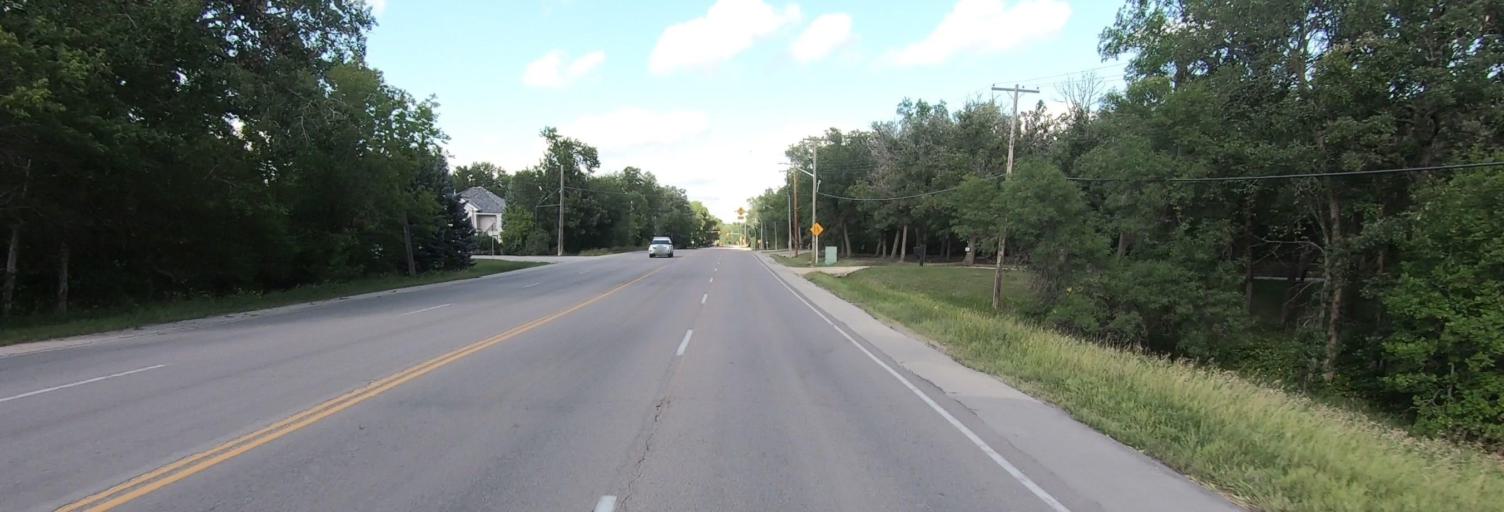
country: CA
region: Manitoba
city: Winnipeg
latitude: 49.9877
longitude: -97.0440
